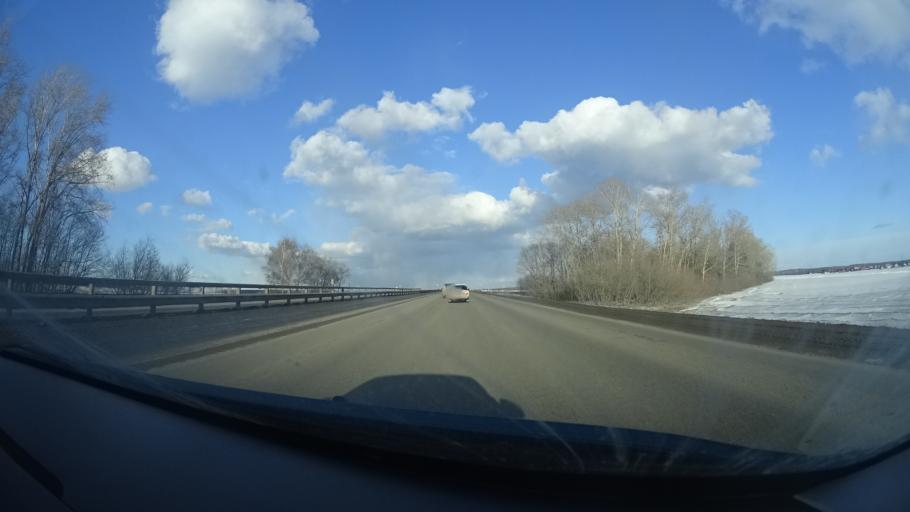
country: RU
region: Bashkortostan
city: Avdon
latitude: 54.6690
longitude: 55.7588
